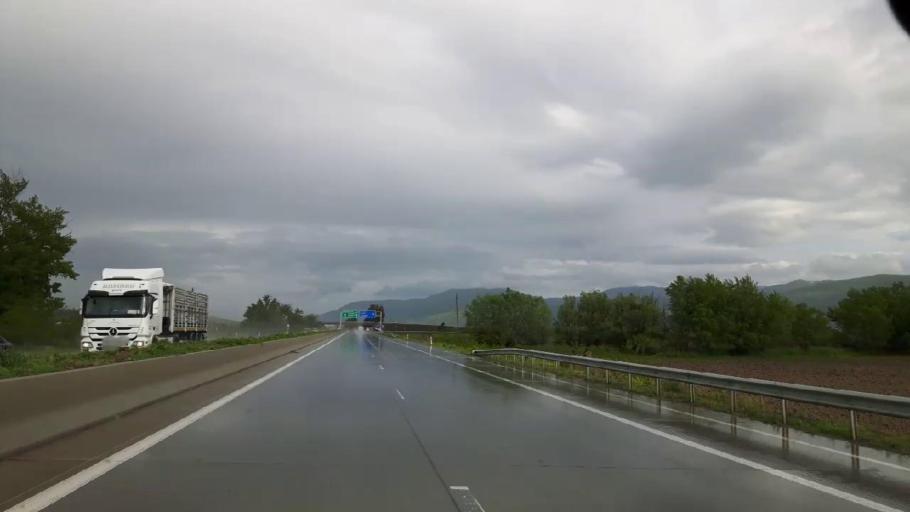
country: GE
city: Agara
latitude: 42.0342
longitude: 43.9431
